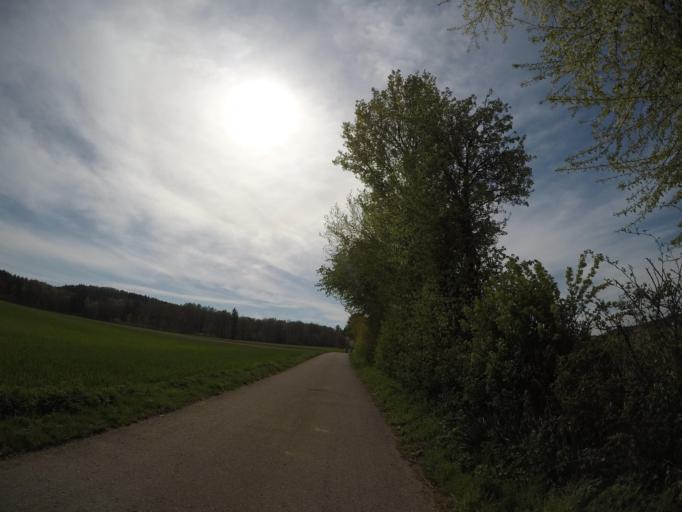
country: DE
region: Baden-Wuerttemberg
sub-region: Tuebingen Region
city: Boms
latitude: 47.9970
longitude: 9.5188
